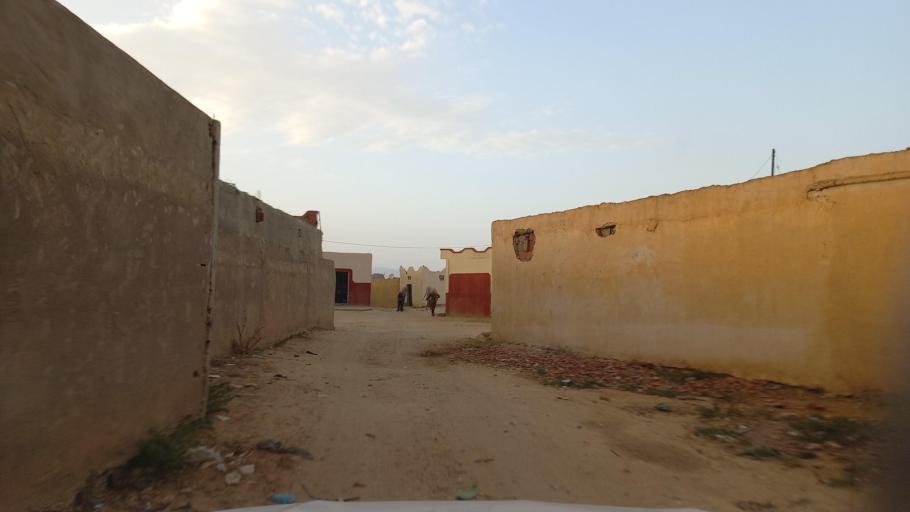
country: TN
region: Al Qasrayn
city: Kasserine
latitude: 35.2657
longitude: 9.0576
